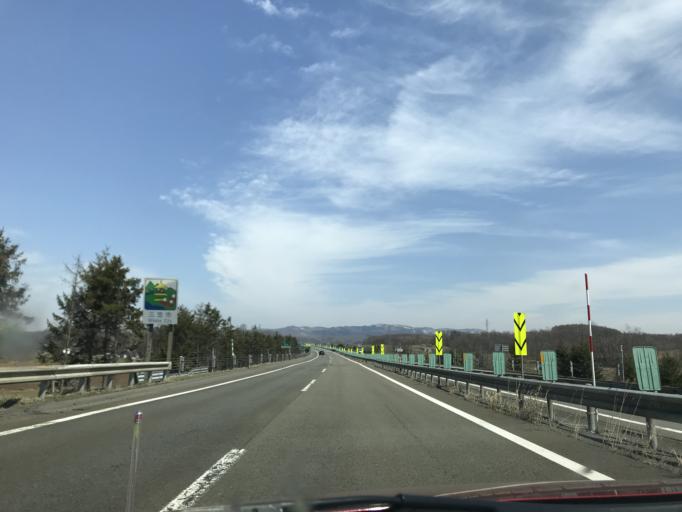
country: JP
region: Hokkaido
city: Iwamizawa
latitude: 43.2175
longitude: 141.8248
